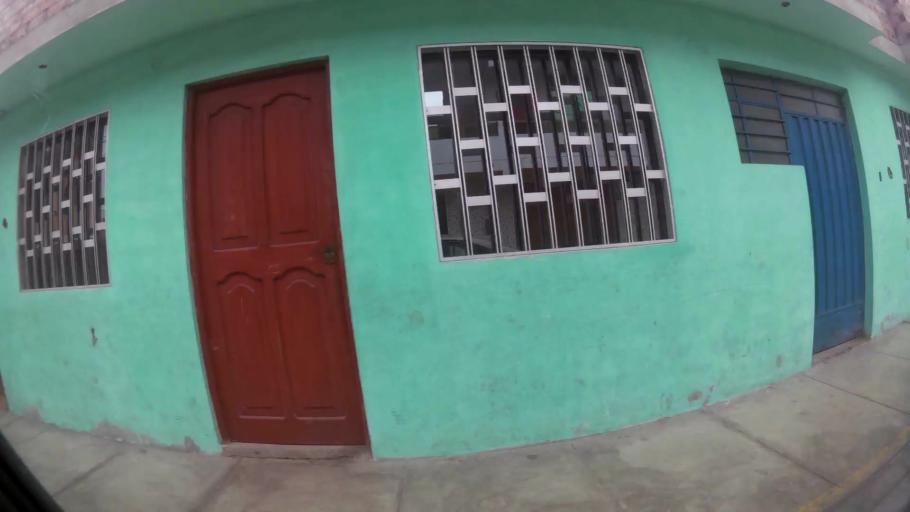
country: PE
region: Lima
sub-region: Provincia de Huaral
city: Chancay
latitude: -11.5557
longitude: -77.2689
